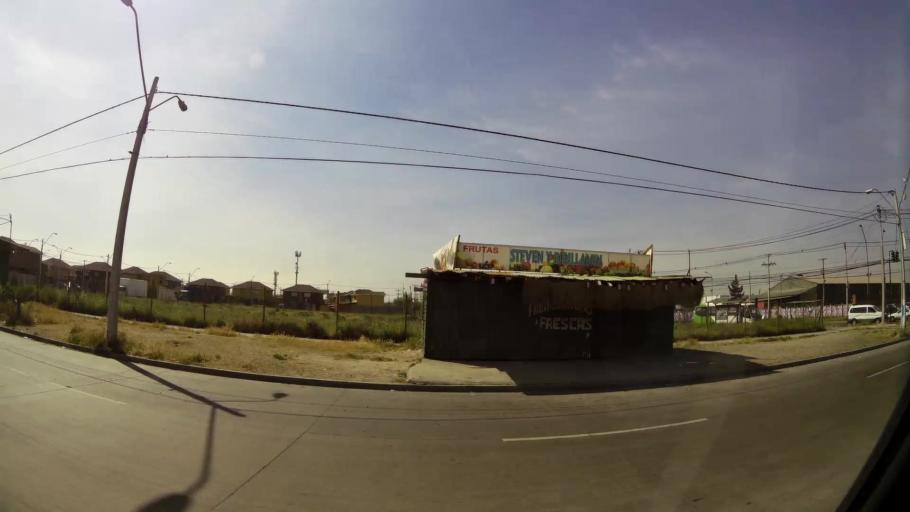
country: CL
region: Santiago Metropolitan
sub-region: Provincia de Santiago
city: Lo Prado
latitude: -33.4433
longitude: -70.7733
